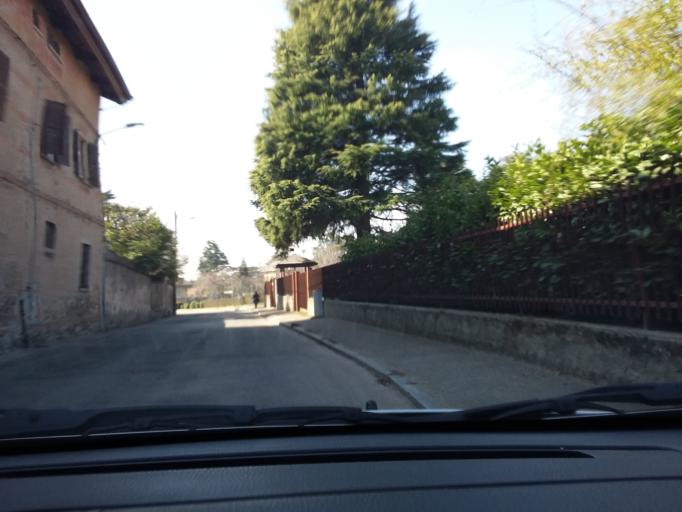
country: IT
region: Piedmont
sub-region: Provincia di Torino
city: Rivoli
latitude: 45.0791
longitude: 7.5252
